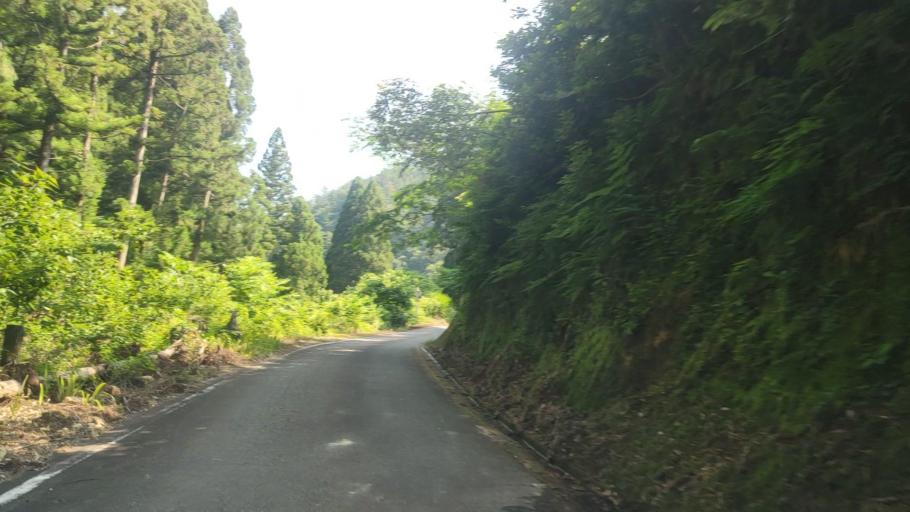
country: JP
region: Ishikawa
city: Komatsu
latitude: 36.2982
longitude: 136.5282
